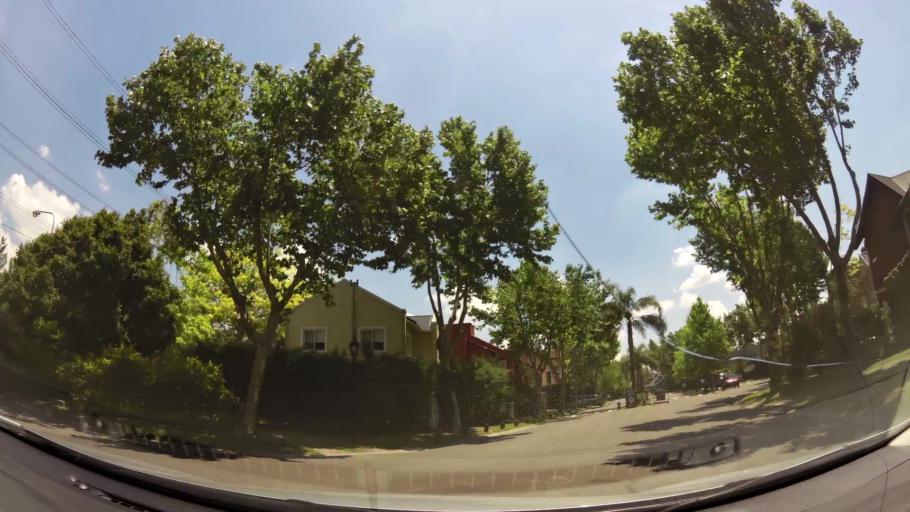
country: AR
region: Buenos Aires
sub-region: Partido de Tigre
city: Tigre
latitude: -34.4287
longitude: -58.5991
